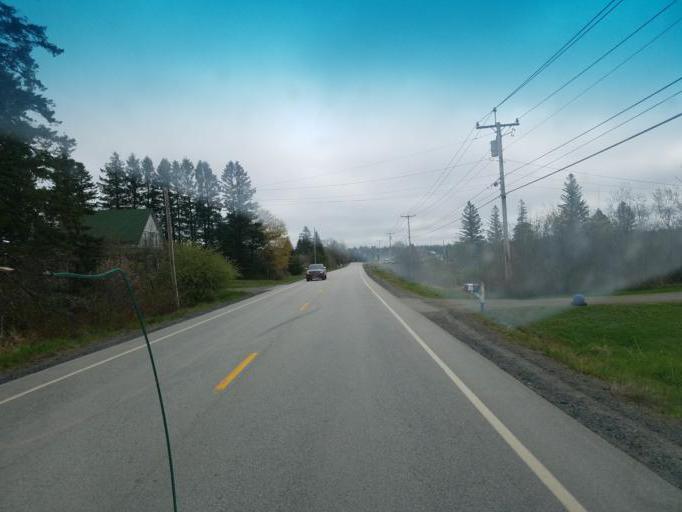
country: US
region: Maine
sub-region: Washington County
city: Eastport
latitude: 44.8183
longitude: -67.0602
